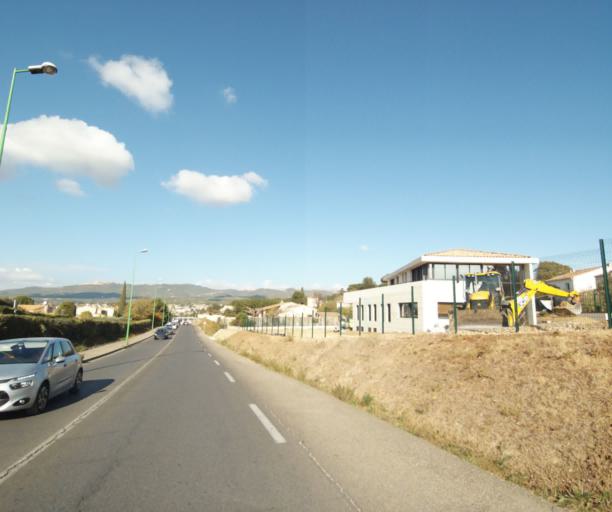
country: FR
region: Provence-Alpes-Cote d'Azur
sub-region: Departement des Bouches-du-Rhone
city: Allauch
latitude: 43.3393
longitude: 5.4740
